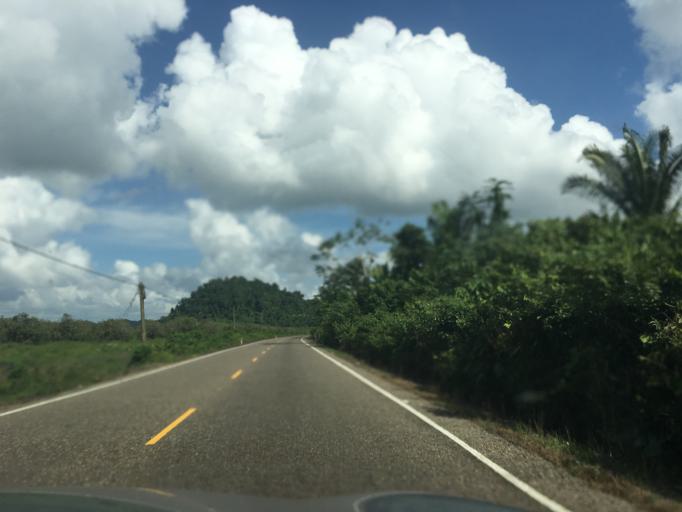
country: BZ
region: Cayo
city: Belmopan
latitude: 17.1531
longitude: -88.6927
